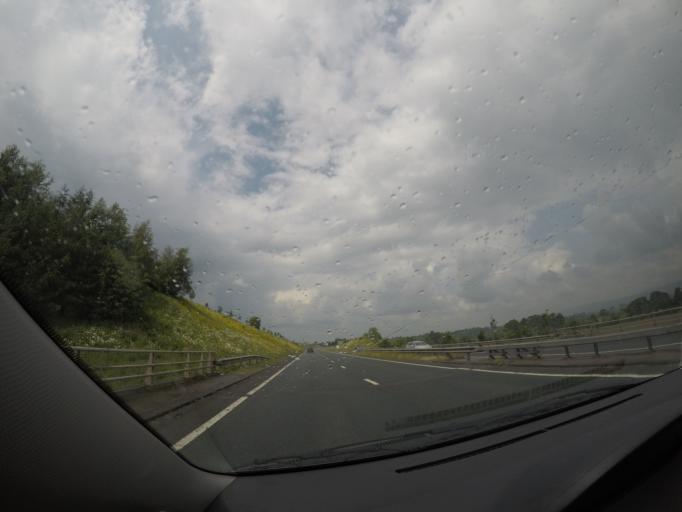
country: GB
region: England
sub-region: Cumbria
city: Appleby-in-Westmorland
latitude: 54.6408
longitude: -2.6156
